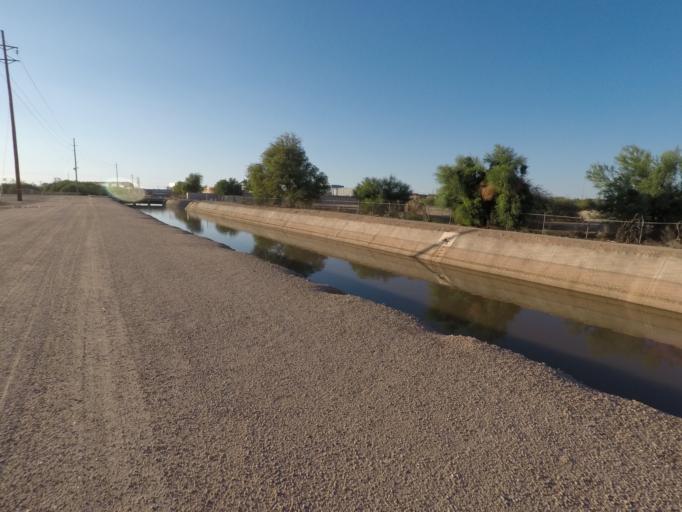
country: US
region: Arizona
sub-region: Maricopa County
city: Tempe Junction
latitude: 33.4443
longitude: -111.9827
